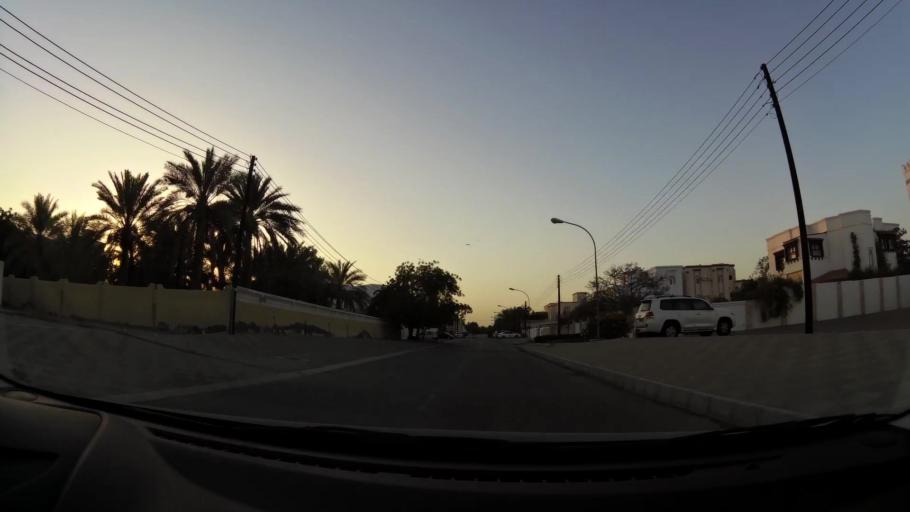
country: OM
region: Muhafazat Masqat
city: As Sib al Jadidah
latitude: 23.6443
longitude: 58.2065
